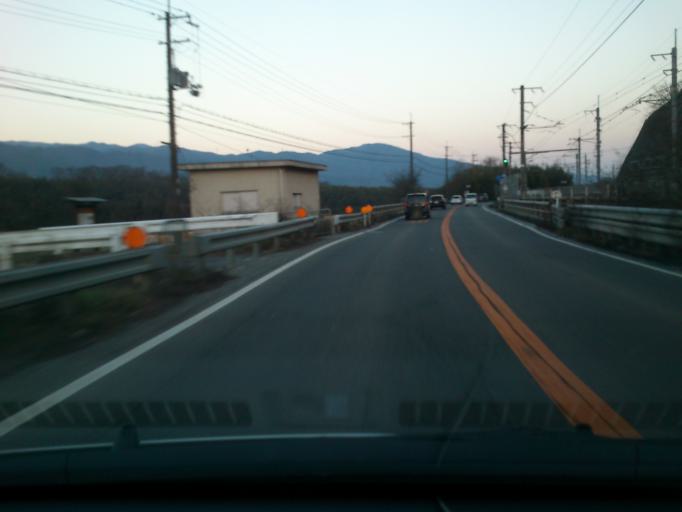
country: JP
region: Kyoto
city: Kameoka
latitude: 35.0667
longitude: 135.5389
